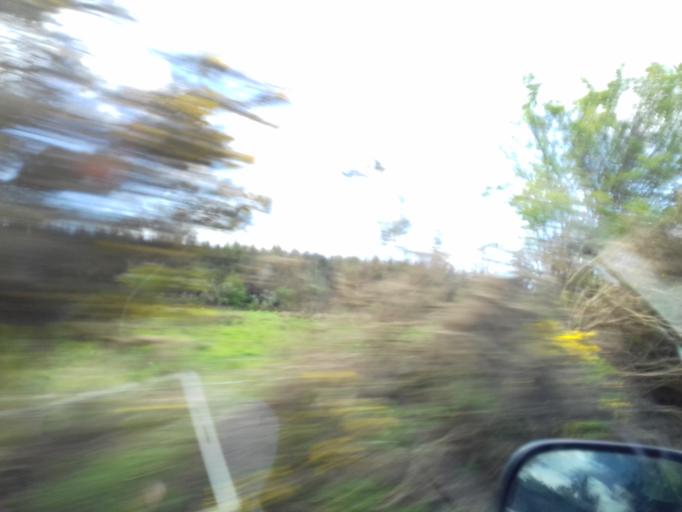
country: IE
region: Leinster
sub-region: Loch Garman
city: Loch Garman
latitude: 52.2825
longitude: -6.6710
